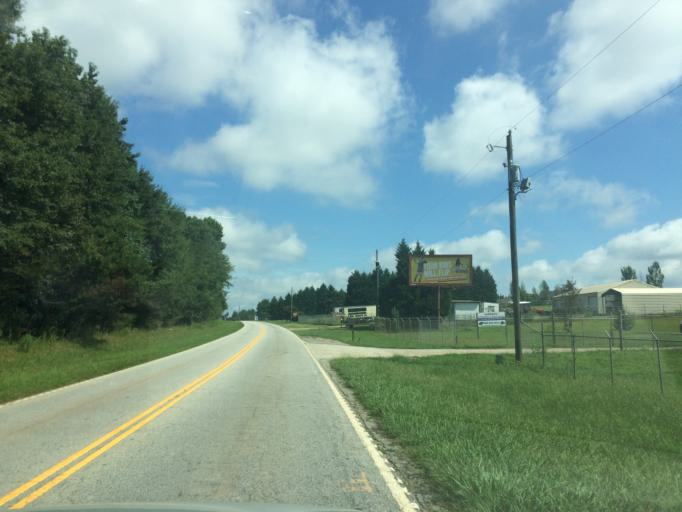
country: US
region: South Carolina
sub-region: Spartanburg County
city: Wellford
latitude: 34.9869
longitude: -82.1110
